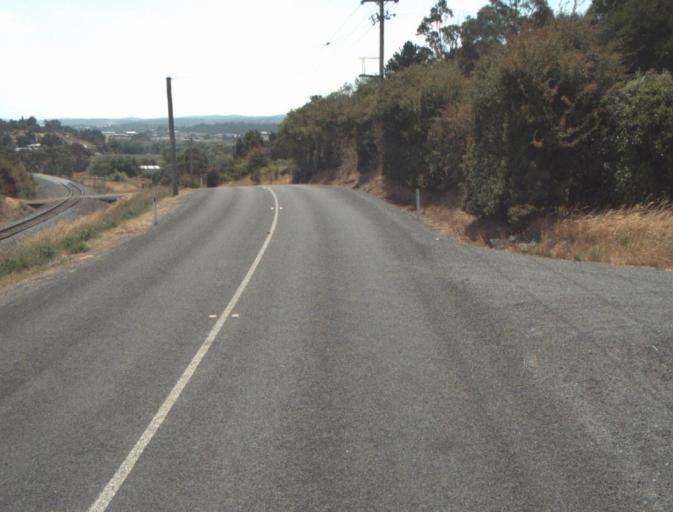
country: AU
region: Tasmania
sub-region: Launceston
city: Newstead
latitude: -41.4711
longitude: 147.1885
